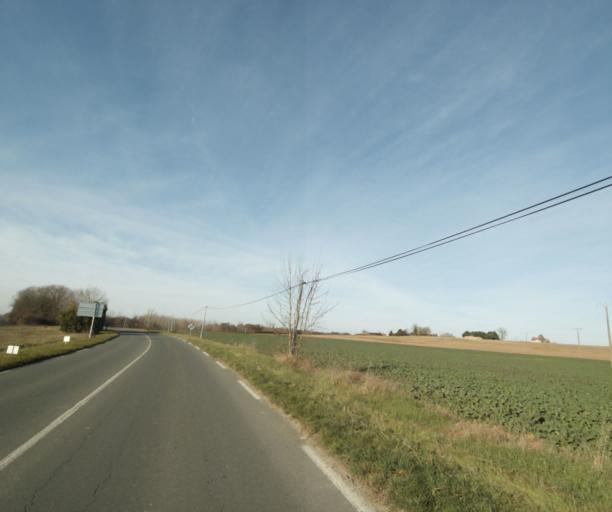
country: FR
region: Poitou-Charentes
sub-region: Departement de la Charente-Maritime
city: Chaniers
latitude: 45.7098
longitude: -0.5312
